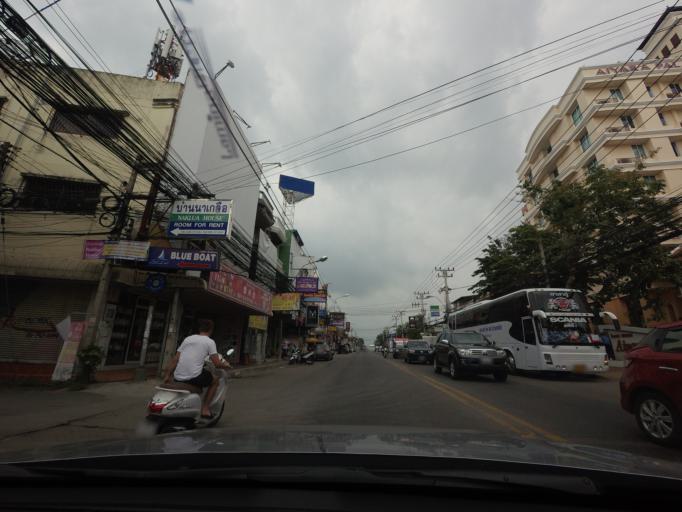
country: TH
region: Chon Buri
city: Phatthaya
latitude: 12.9567
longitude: 100.8916
